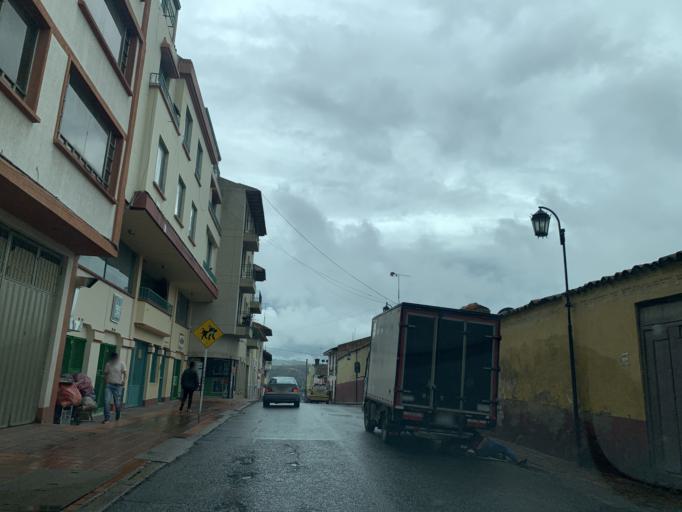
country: CO
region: Boyaca
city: Tunja
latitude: 5.5307
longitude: -73.3612
